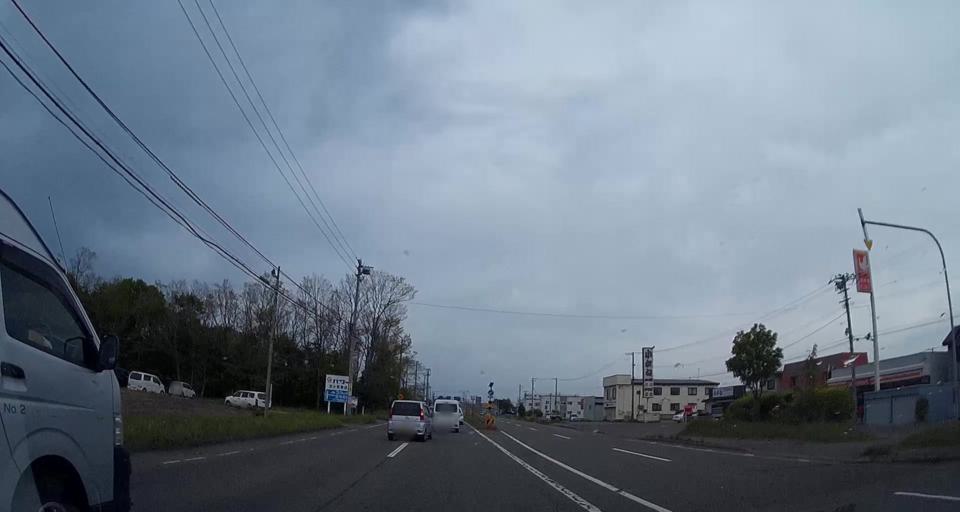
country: JP
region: Hokkaido
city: Tomakomai
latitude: 42.6710
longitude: 141.7019
